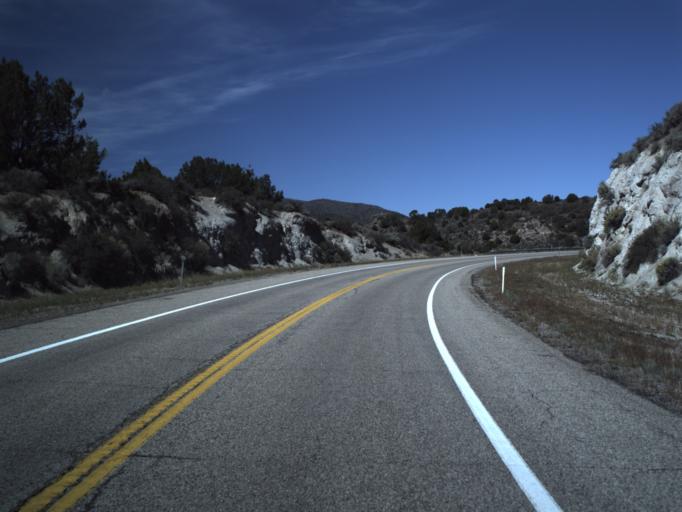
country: US
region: Utah
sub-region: Washington County
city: Enterprise
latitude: 37.4647
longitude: -113.6349
